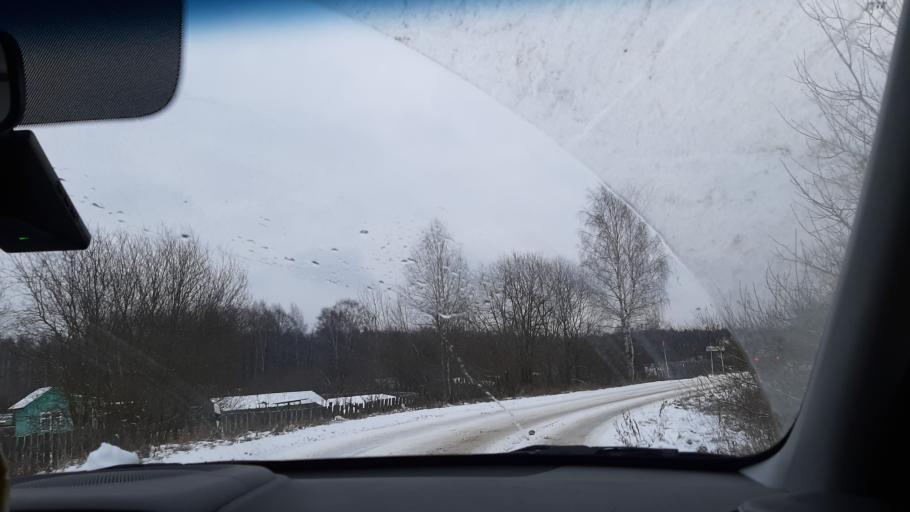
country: RU
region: Ivanovo
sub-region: Gorod Ivanovo
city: Ivanovo
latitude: 56.9287
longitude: 40.9799
